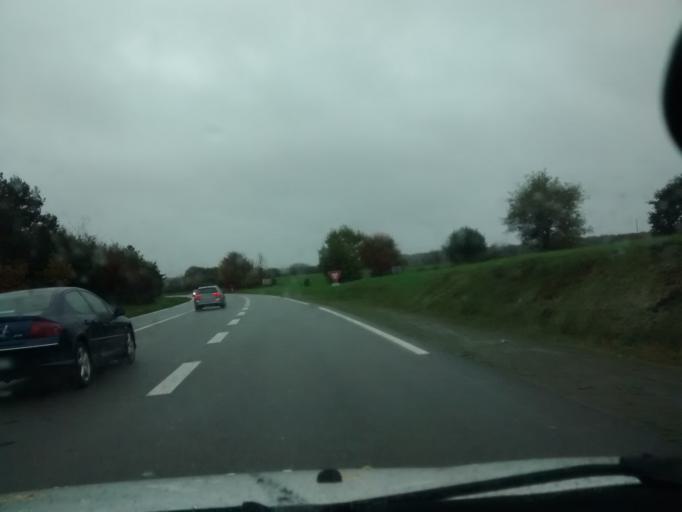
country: FR
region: Brittany
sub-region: Departement d'Ille-et-Vilaine
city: Chantepie
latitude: 48.0834
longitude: -1.6220
